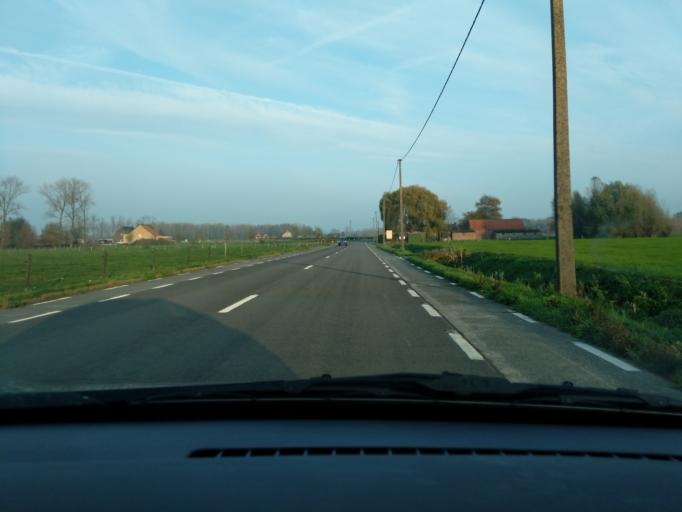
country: BE
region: Flanders
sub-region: Provincie West-Vlaanderen
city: Ruiselede
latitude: 51.0447
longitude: 3.4323
